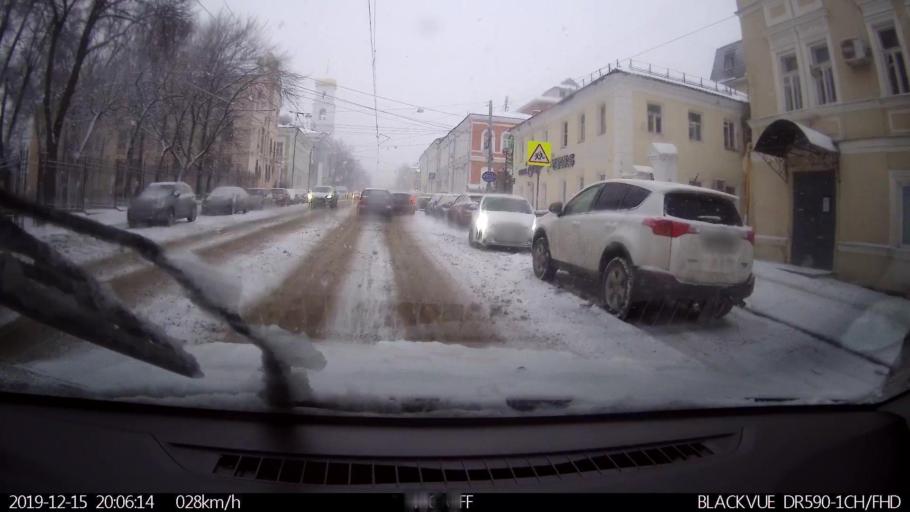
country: RU
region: Nizjnij Novgorod
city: Nizhniy Novgorod
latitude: 56.3229
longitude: 43.9908
